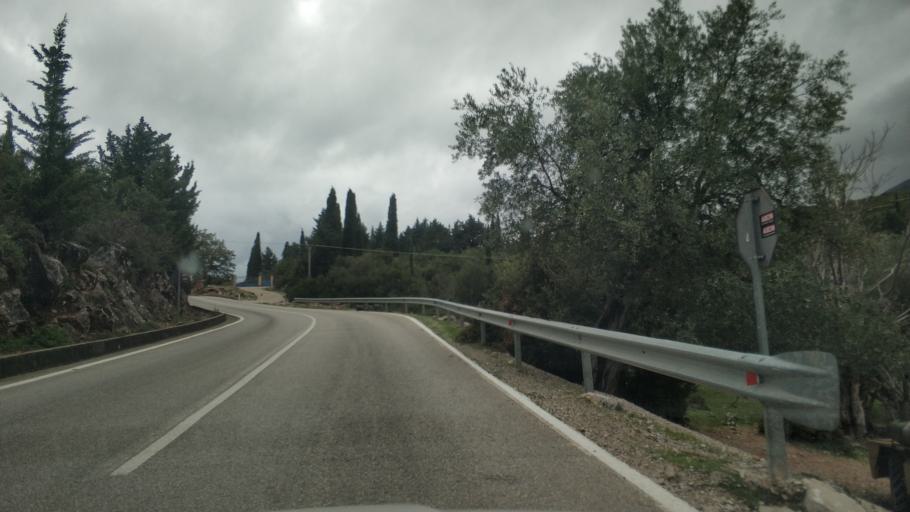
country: AL
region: Vlore
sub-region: Rrethi i Vlores
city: Vranisht
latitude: 40.1421
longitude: 19.6719
